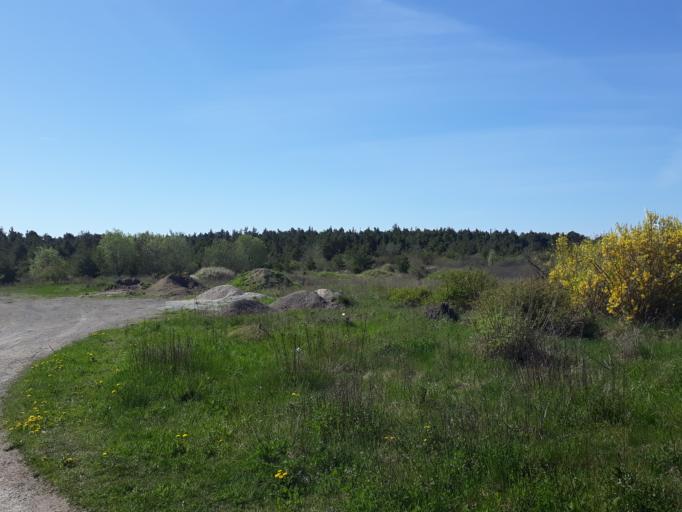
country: SE
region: Gotland
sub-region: Gotland
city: Klintehamn
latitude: 57.3820
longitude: 18.2039
